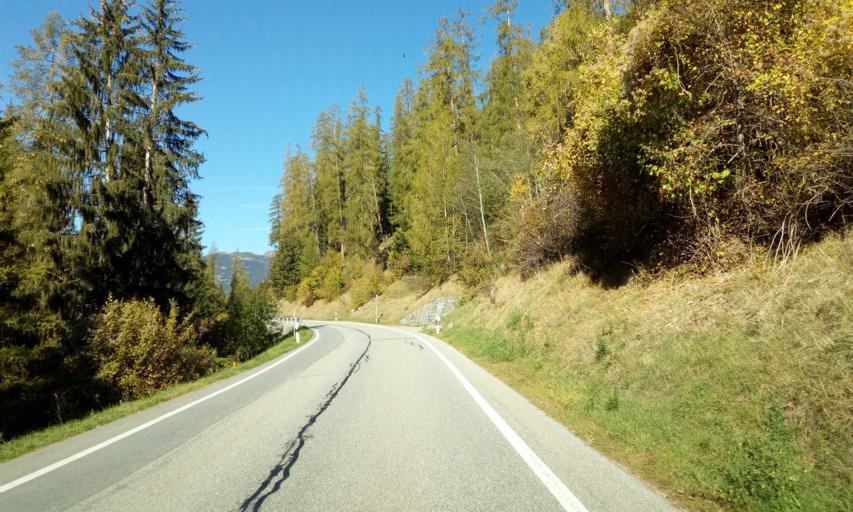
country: CH
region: Grisons
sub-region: Albula District
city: Tiefencastel
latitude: 46.6707
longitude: 9.5831
